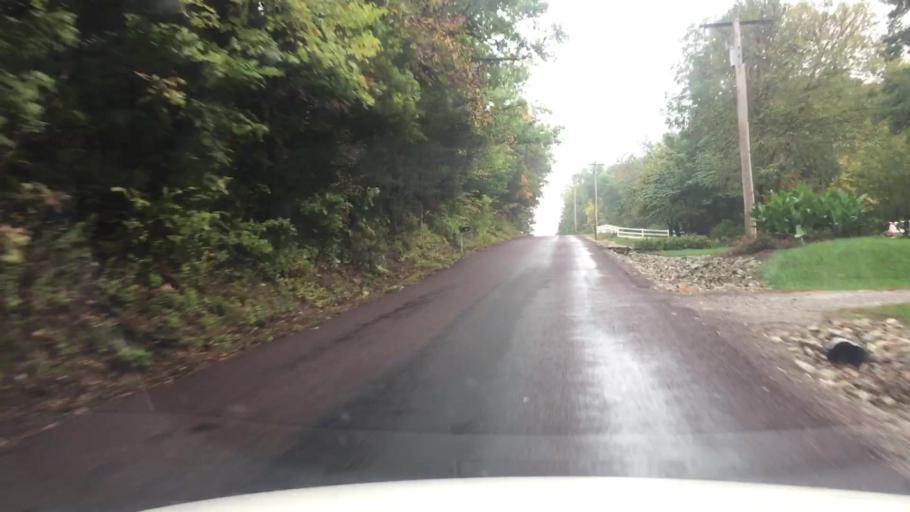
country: US
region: Missouri
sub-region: Boone County
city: Columbia
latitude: 38.8560
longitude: -92.3679
